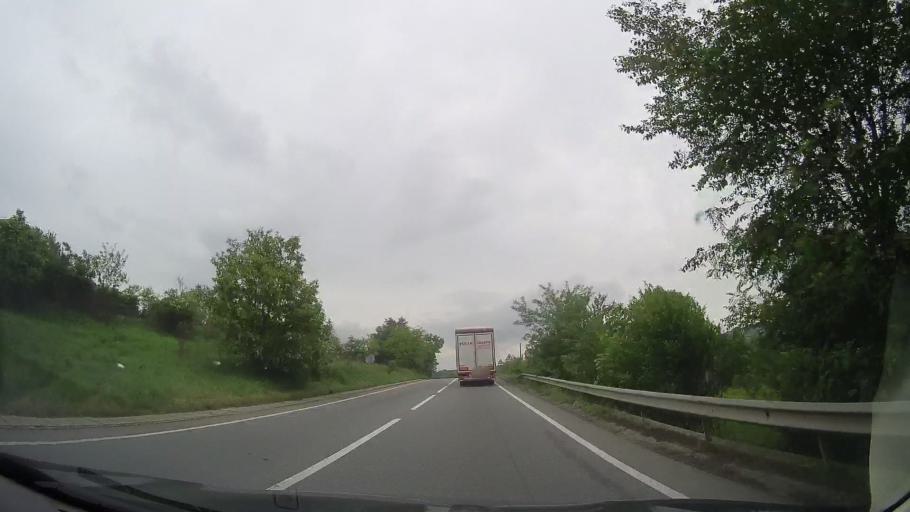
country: RO
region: Caras-Severin
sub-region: Comuna Cornea
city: Cornea
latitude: 45.0036
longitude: 22.3207
